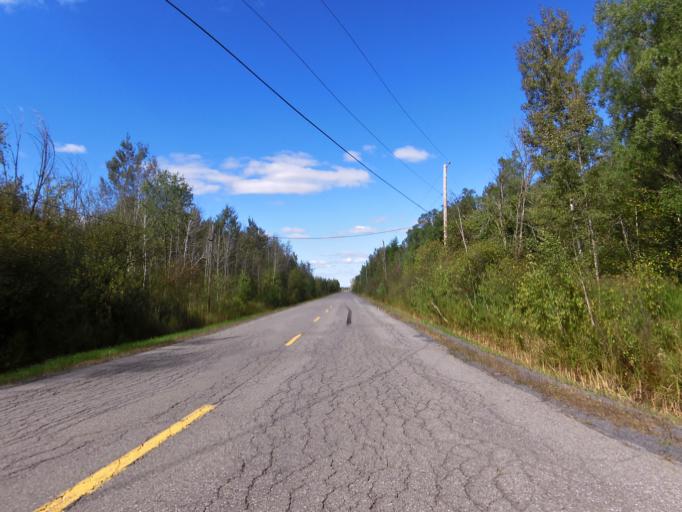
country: CA
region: Ontario
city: Ottawa
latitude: 45.3195
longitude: -75.4850
